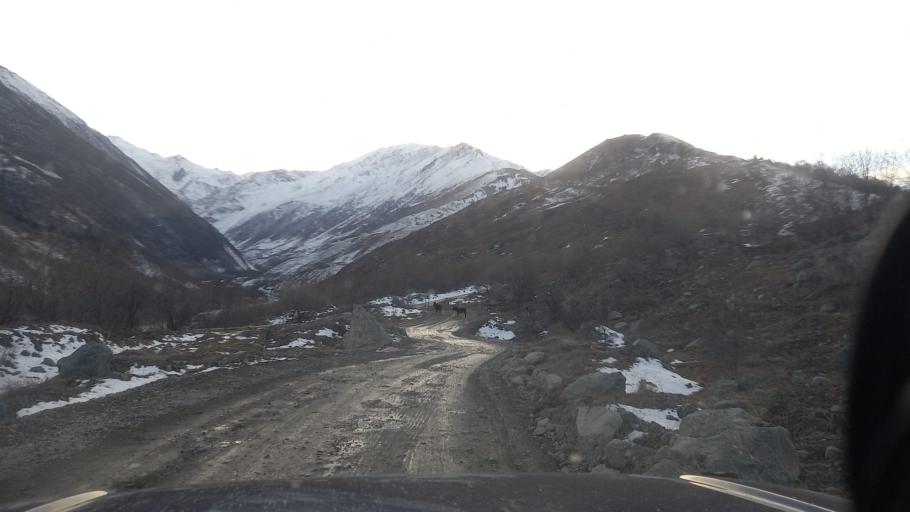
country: RU
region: Ingushetiya
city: Dzhayrakh
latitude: 42.8397
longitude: 44.5117
